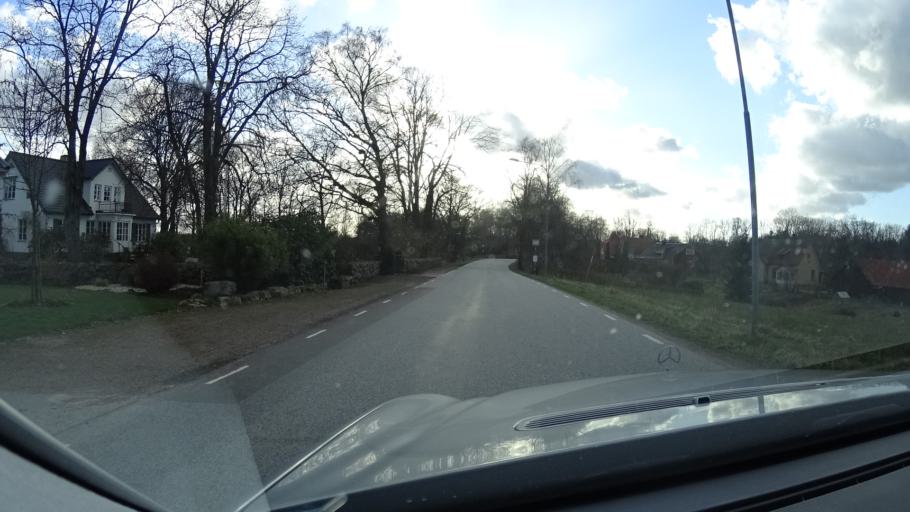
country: SE
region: Skane
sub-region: Hoors Kommun
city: Satofta
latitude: 55.9030
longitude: 13.6014
